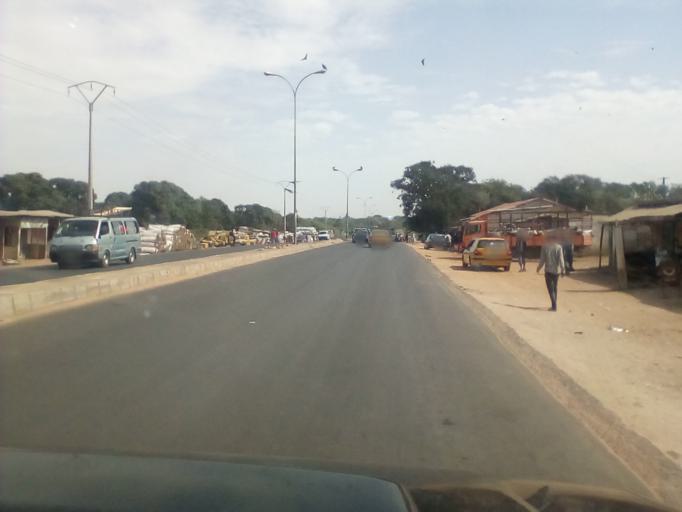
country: GM
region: Western
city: Abuko
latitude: 13.3999
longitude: -16.6514
